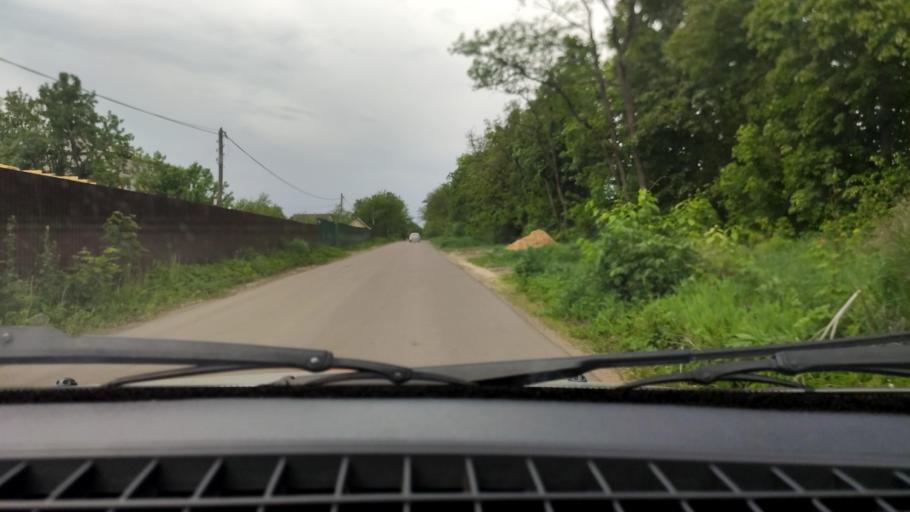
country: RU
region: Voronezj
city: Shilovo
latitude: 51.5976
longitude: 39.1302
